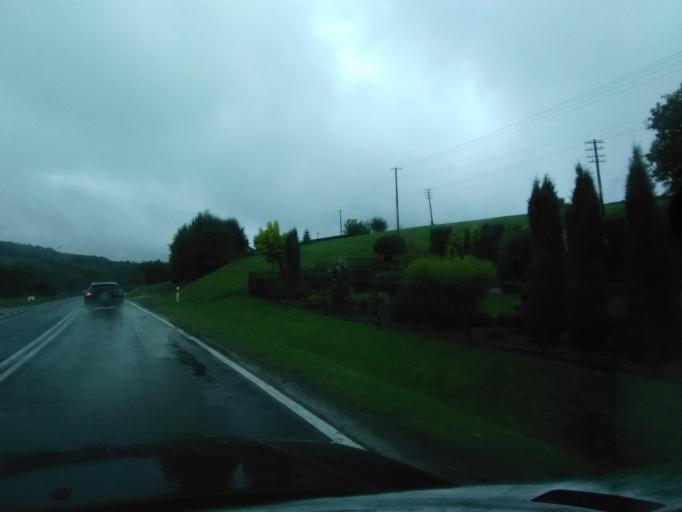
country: PL
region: Subcarpathian Voivodeship
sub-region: Powiat ropczycko-sedziszowski
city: Niedzwiada
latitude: 50.0051
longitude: 21.5564
